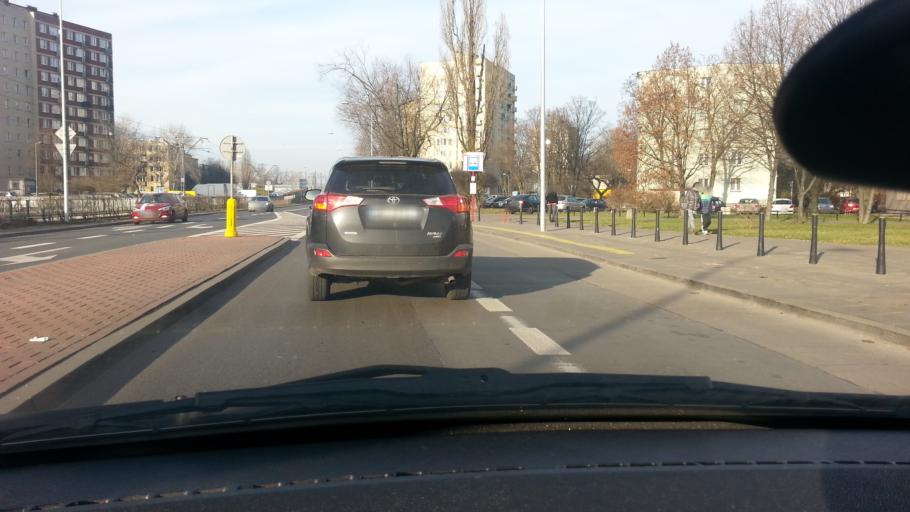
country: PL
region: Masovian Voivodeship
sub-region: Warszawa
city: Targowek
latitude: 52.2939
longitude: 21.0270
